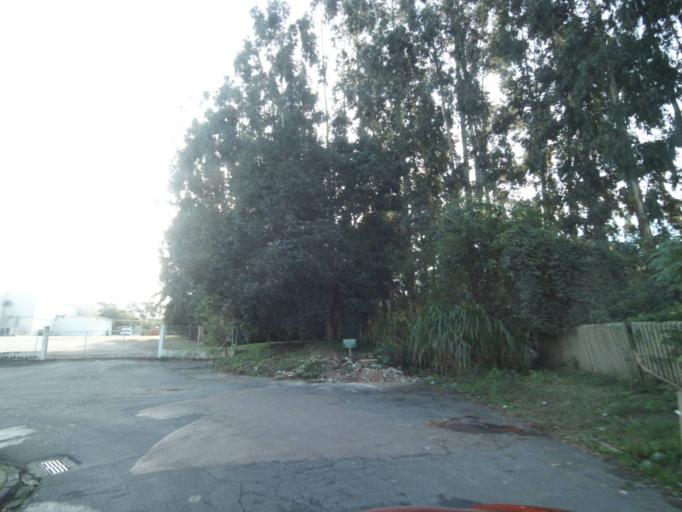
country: BR
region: Parana
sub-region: Curitiba
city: Curitiba
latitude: -25.4328
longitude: -49.3099
